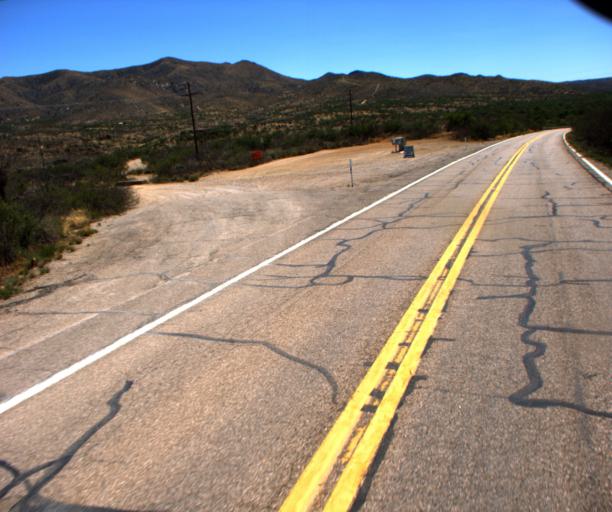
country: US
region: Arizona
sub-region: Pima County
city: Corona de Tucson
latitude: 31.9202
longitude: -110.6572
